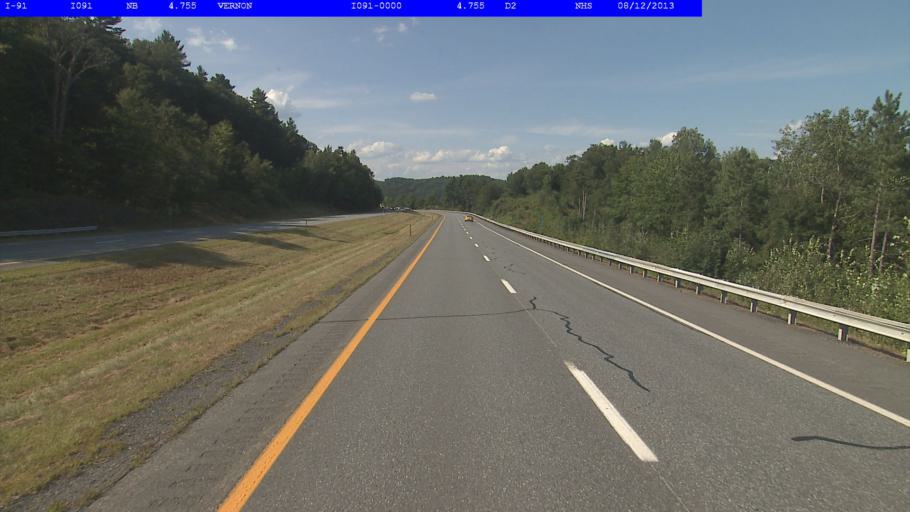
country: US
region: Vermont
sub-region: Windham County
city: Brattleboro
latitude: 42.7983
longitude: -72.5618
